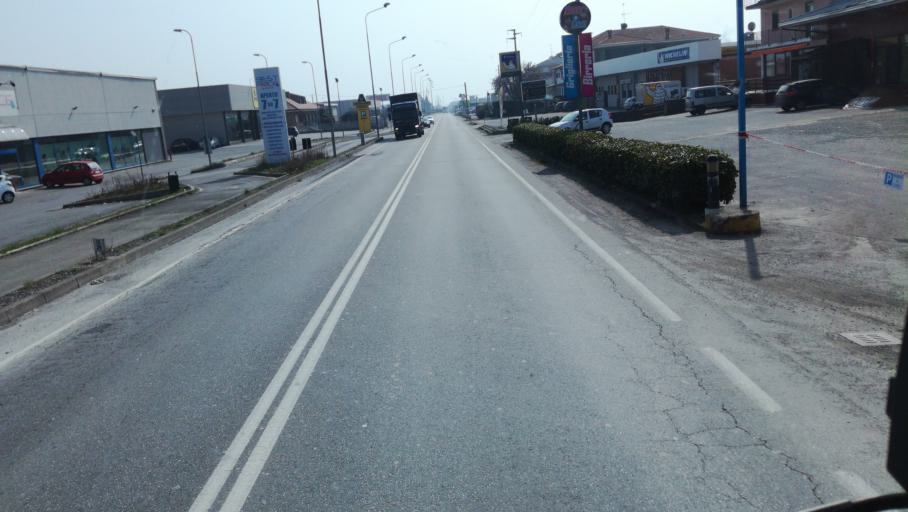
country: IT
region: Piedmont
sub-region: Provincia di Novara
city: Romagnano Sesia
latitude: 45.6215
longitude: 8.4002
